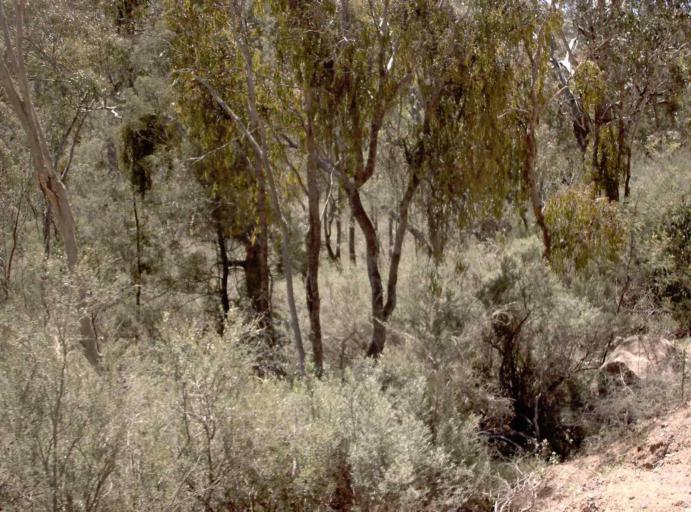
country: AU
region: New South Wales
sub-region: Snowy River
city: Jindabyne
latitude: -37.0396
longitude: 148.5386
